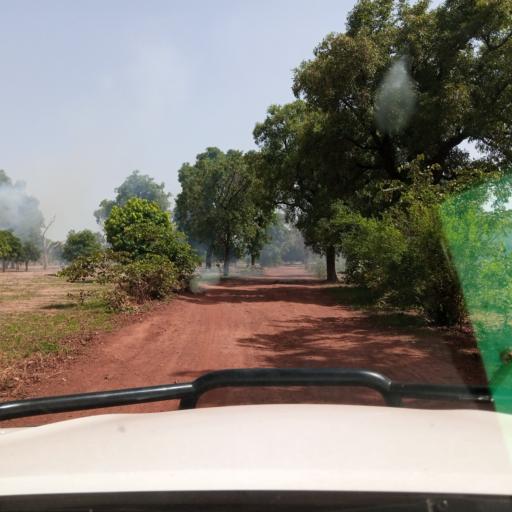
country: ML
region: Koulikoro
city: Kangaba
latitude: 12.2527
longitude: -8.6339
